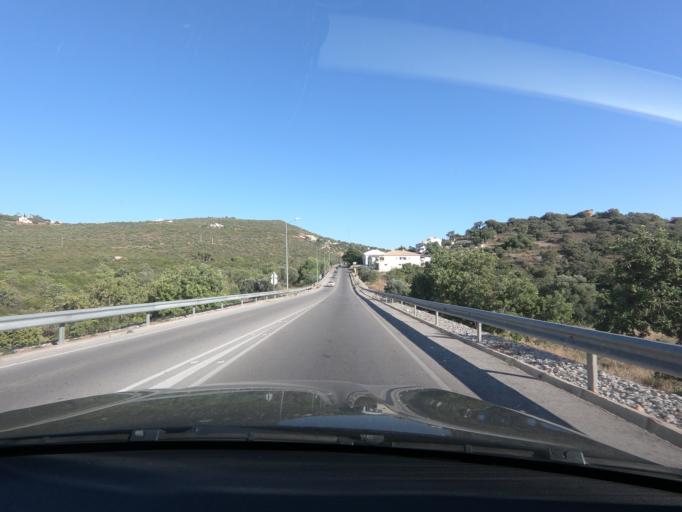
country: PT
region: Faro
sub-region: Loule
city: Loule
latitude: 37.1198
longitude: -8.0123
